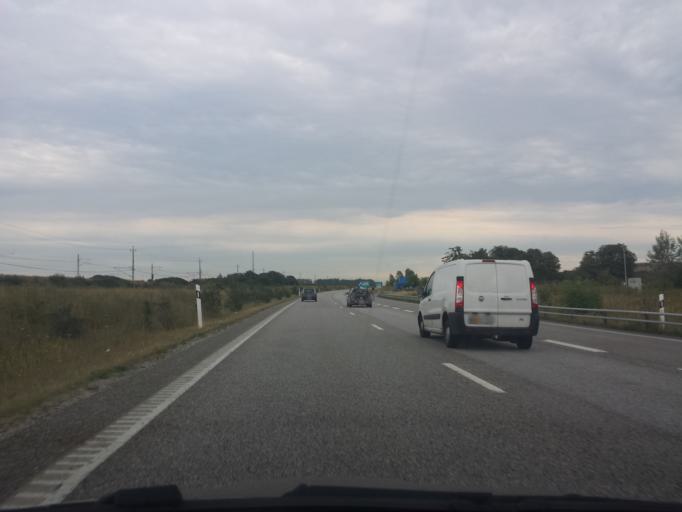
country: SE
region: Skane
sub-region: Malmo
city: Bunkeflostrand
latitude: 55.5615
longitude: 12.9332
